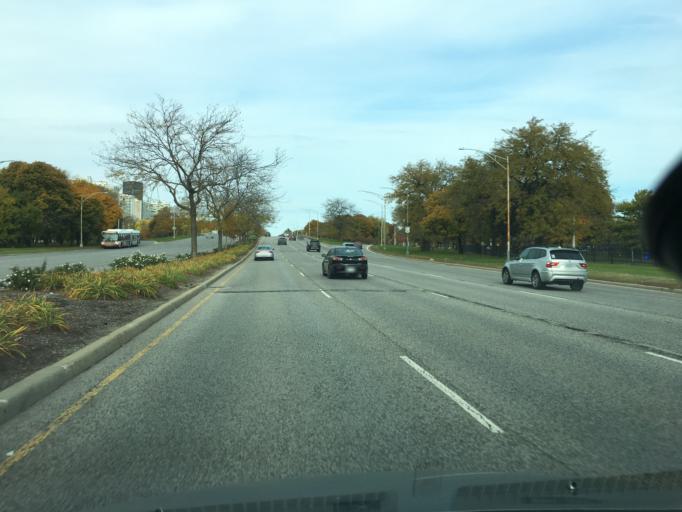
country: US
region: Illinois
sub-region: Cook County
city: Evanston
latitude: 41.9667
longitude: -87.6474
